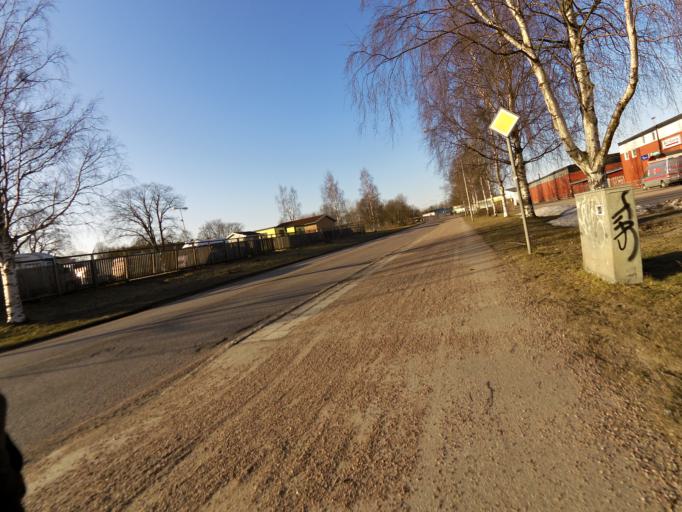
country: SE
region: Gaevleborg
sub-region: Gavle Kommun
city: Gavle
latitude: 60.6738
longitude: 17.1823
